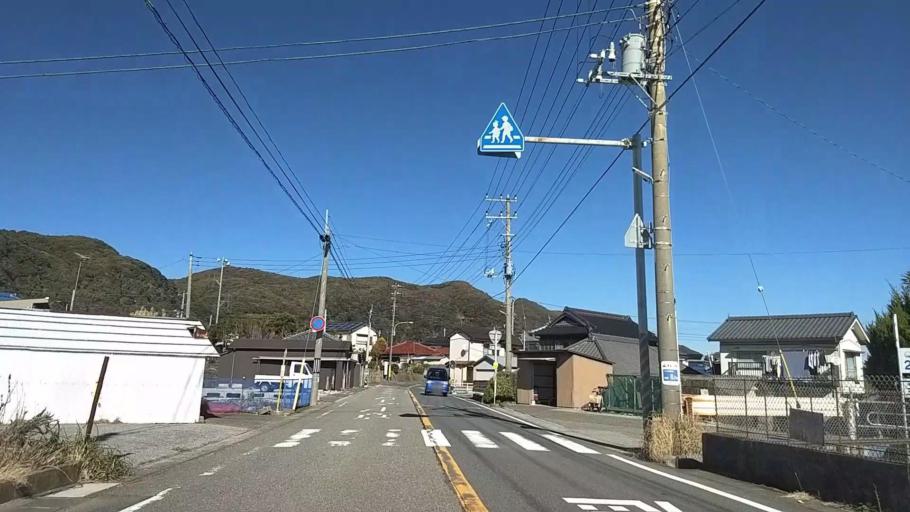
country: JP
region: Chiba
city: Tateyama
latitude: 34.9218
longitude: 139.9389
